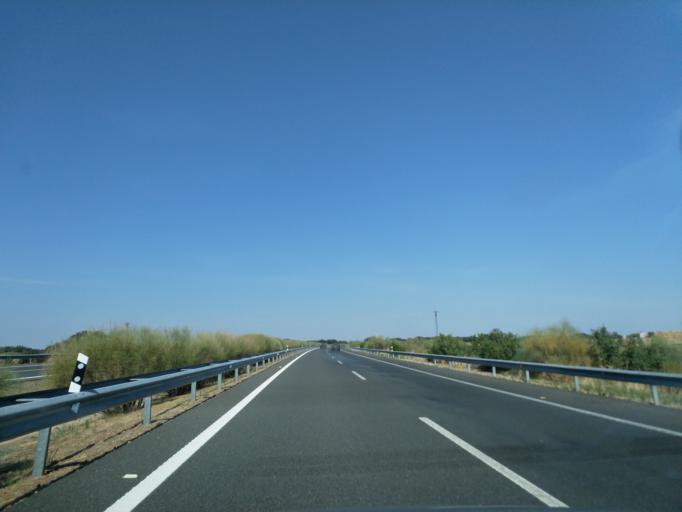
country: ES
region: Extremadura
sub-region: Provincia de Caceres
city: Aldea del Cano
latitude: 39.2649
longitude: -6.3177
